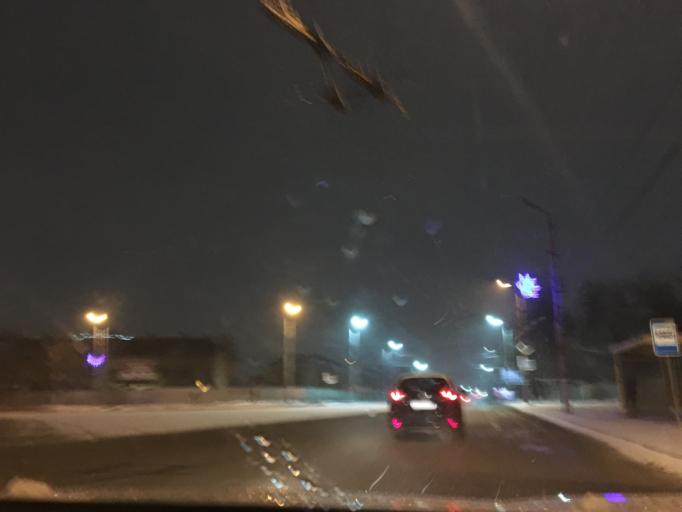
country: RU
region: Tula
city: Tula
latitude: 54.1851
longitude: 37.5726
